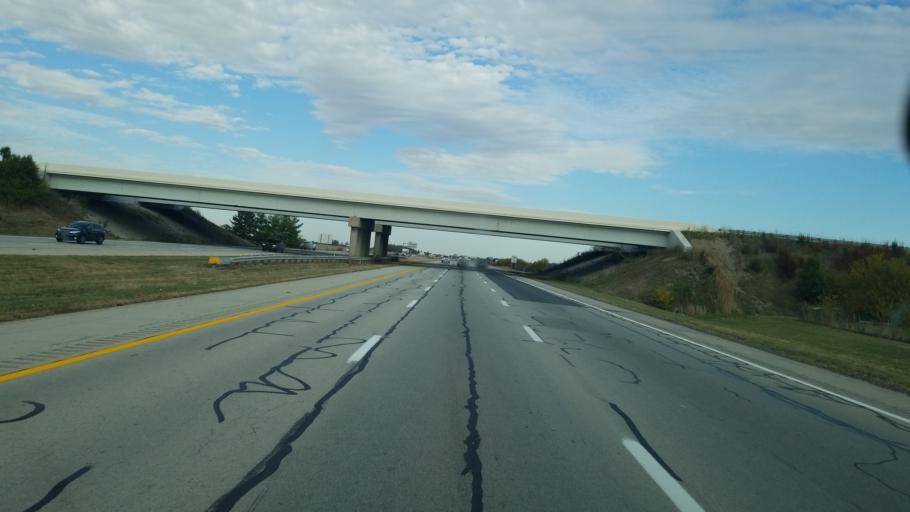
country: US
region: Ohio
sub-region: Fayette County
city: Jeffersonville
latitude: 39.6228
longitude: -83.5986
